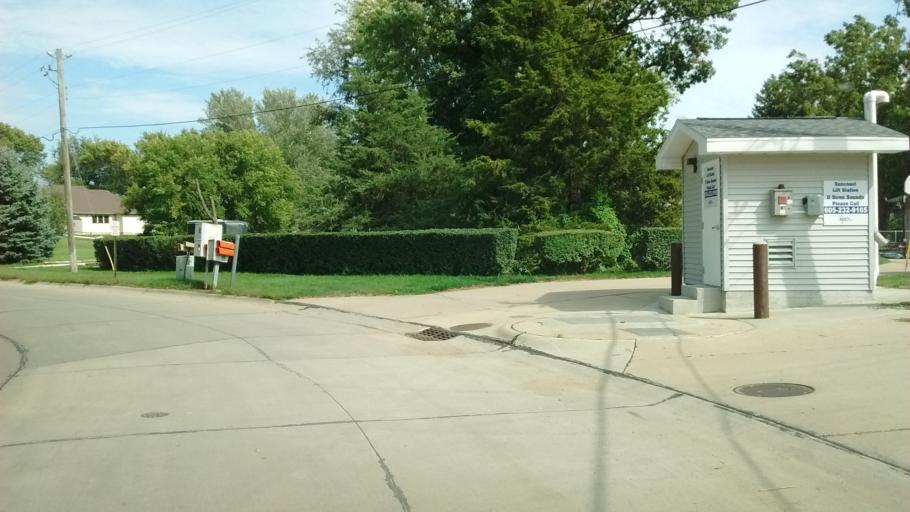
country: US
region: South Dakota
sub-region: Union County
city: North Sioux City
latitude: 42.5465
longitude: -96.5235
